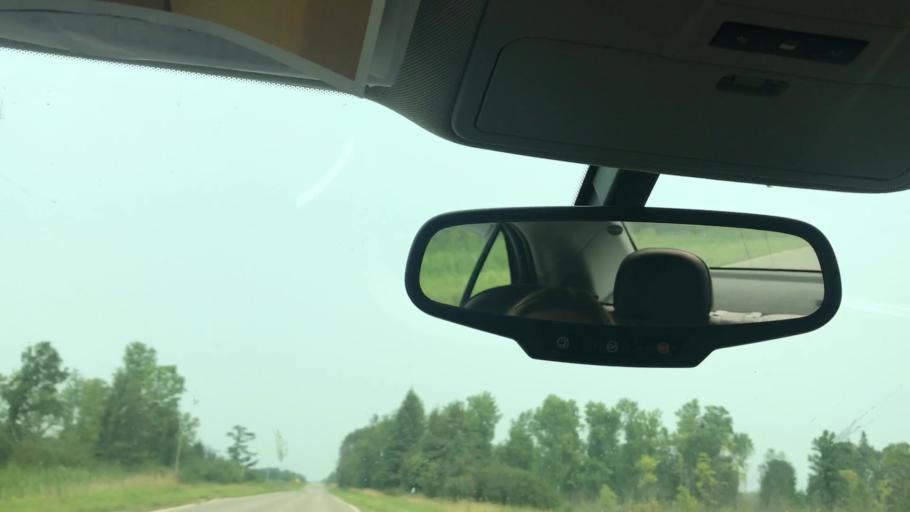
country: US
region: Minnesota
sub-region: Itasca County
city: Cohasset
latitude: 47.3714
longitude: -93.8803
